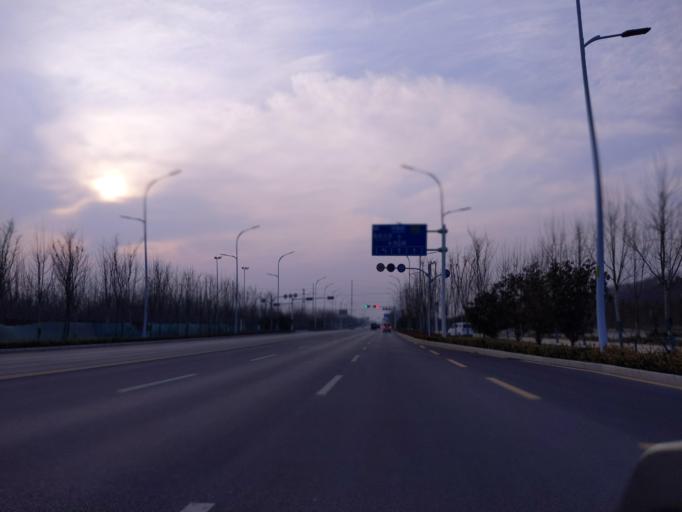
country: CN
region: Henan Sheng
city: Puyang
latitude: 35.8184
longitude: 115.0054
